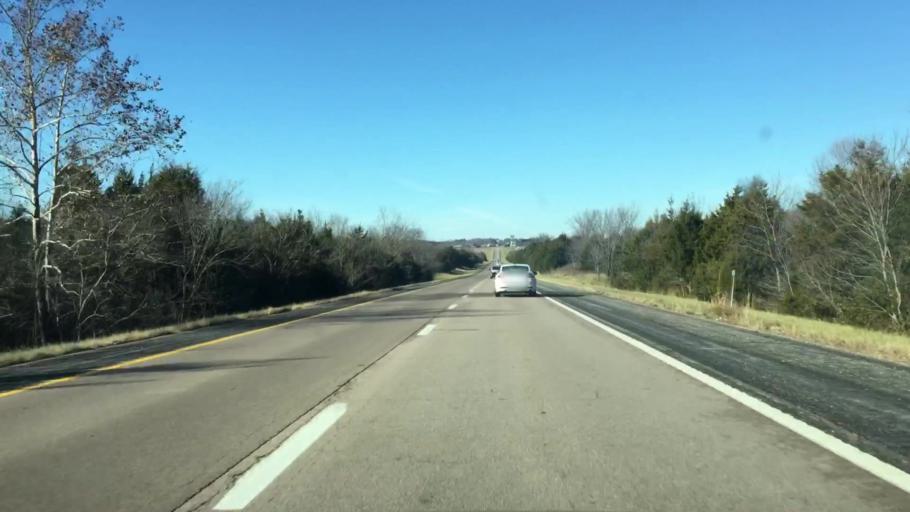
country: US
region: Missouri
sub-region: Miller County
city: Eldon
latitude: 38.3677
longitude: -92.4836
